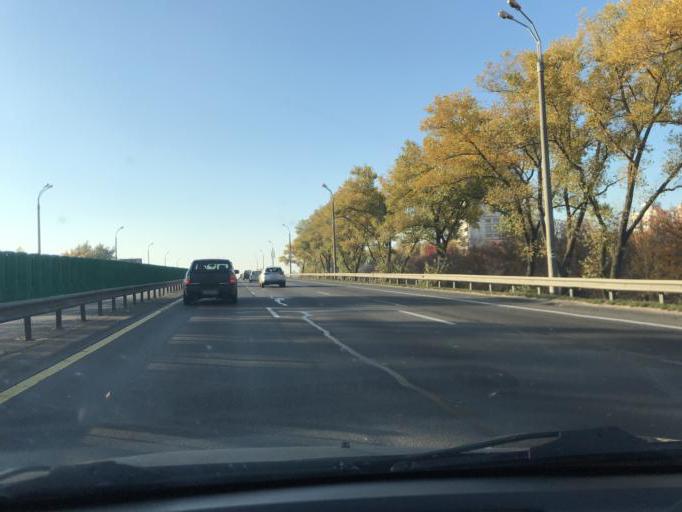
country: BY
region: Minsk
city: Yubilyeyny
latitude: 53.8403
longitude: 27.4888
